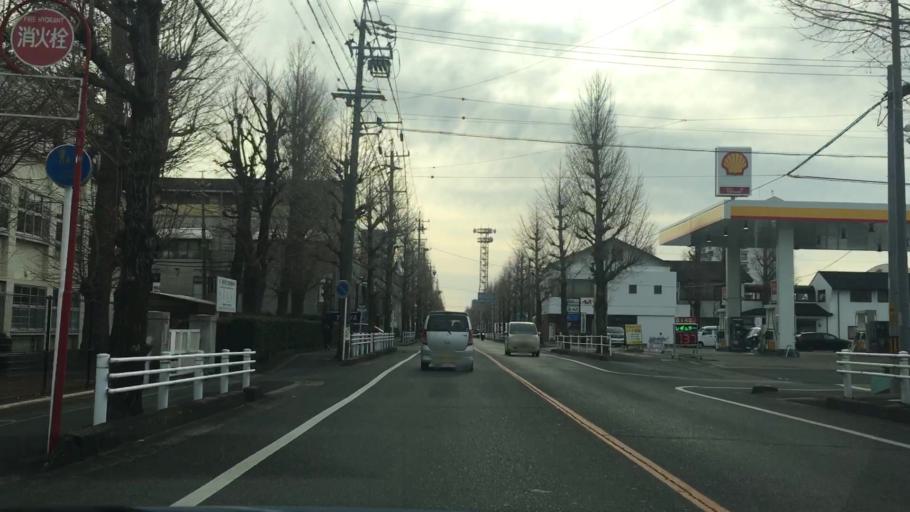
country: JP
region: Aichi
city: Toyohashi
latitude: 34.7385
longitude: 137.3794
